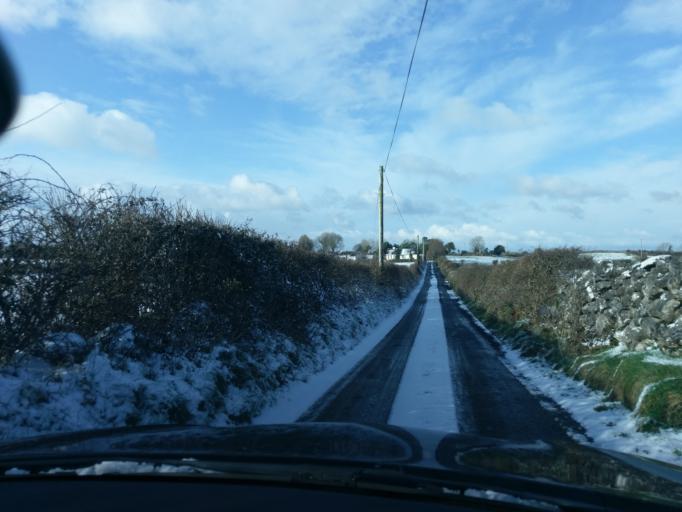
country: IE
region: Connaught
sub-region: County Galway
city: Athenry
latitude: 53.2033
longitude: -8.8099
